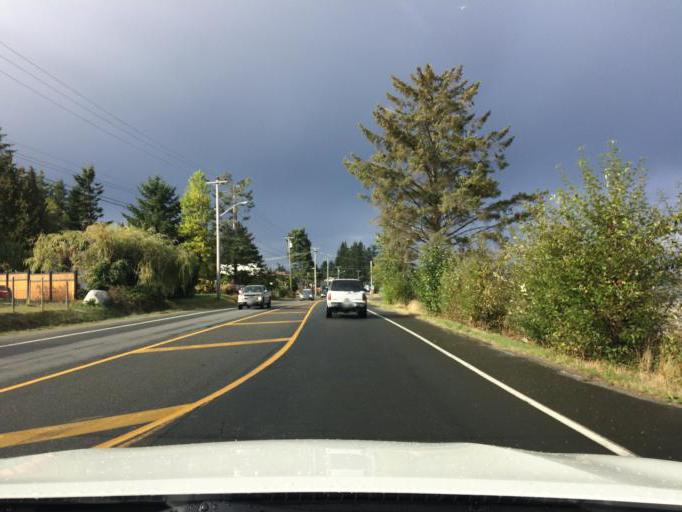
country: CA
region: British Columbia
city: Campbell River
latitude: 49.9549
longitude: -125.2046
